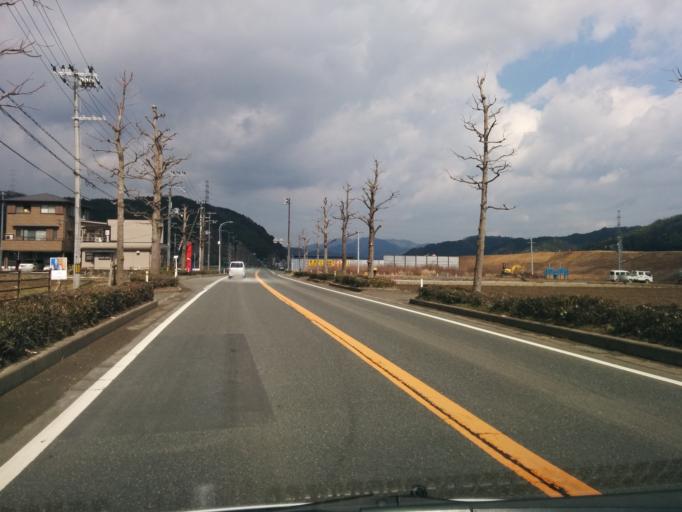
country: JP
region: Kyoto
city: Maizuru
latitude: 35.4329
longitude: 135.2524
